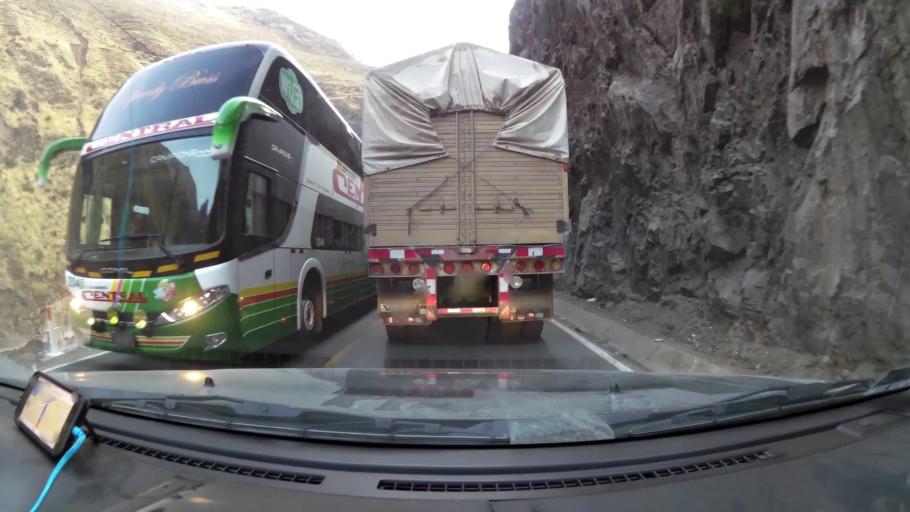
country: PE
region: Lima
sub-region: Provincia de Huarochiri
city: Matucana
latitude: -11.8107
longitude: -76.3451
